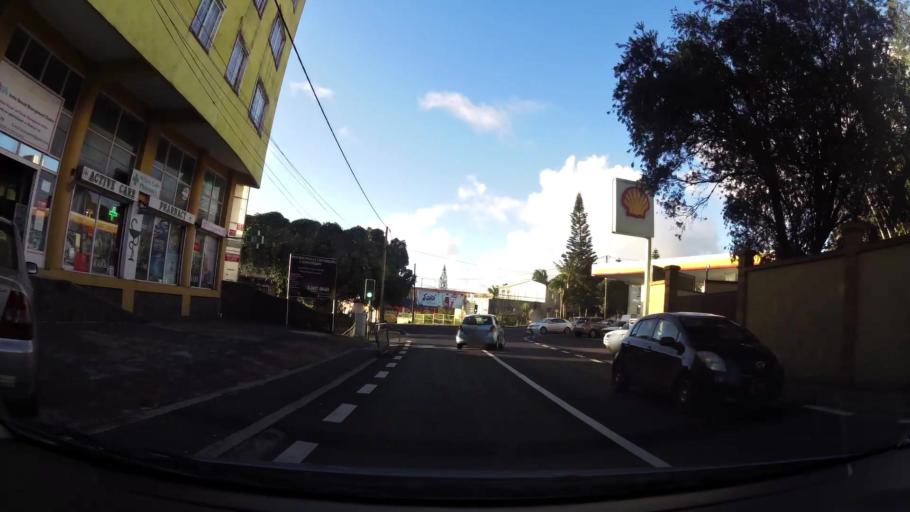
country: MU
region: Plaines Wilhems
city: Curepipe
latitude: -20.3070
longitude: 57.5254
